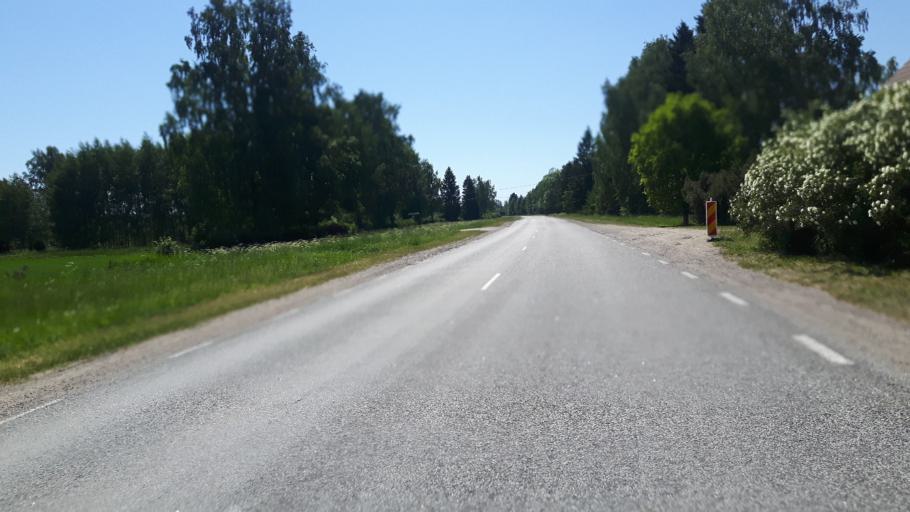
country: EE
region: Paernumaa
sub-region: Tootsi vald
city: Tootsi
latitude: 58.4684
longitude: 24.7893
